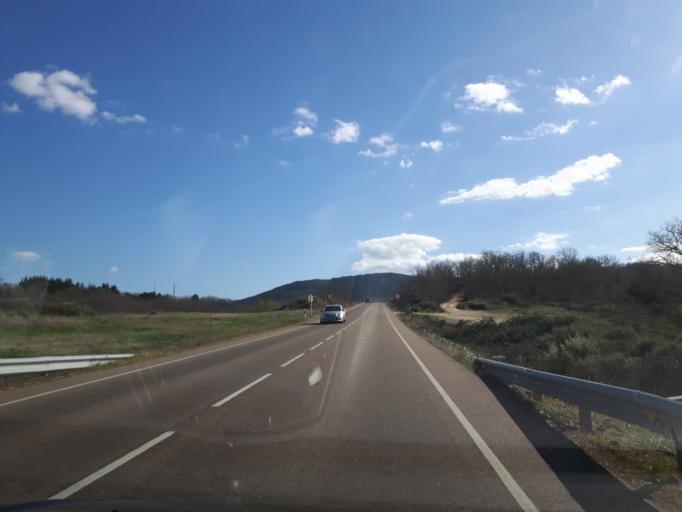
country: ES
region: Castille and Leon
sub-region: Provincia de Salamanca
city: Linares de Riofrio
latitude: 40.5935
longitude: -5.9168
